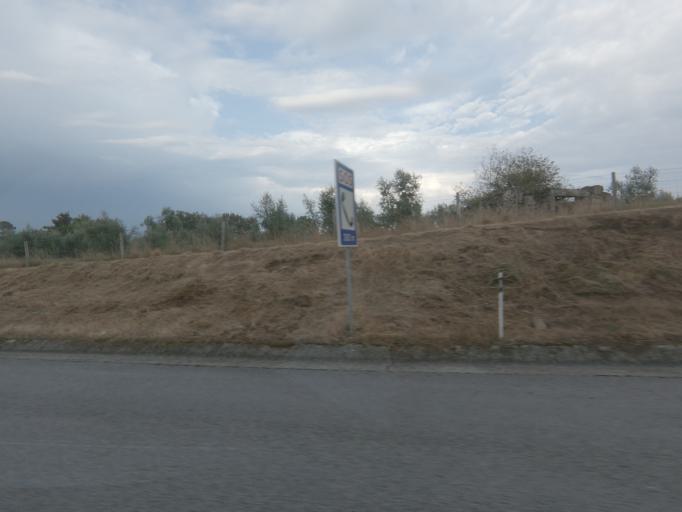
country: PT
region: Viseu
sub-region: Viseu
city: Campo
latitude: 40.7371
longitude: -7.9241
